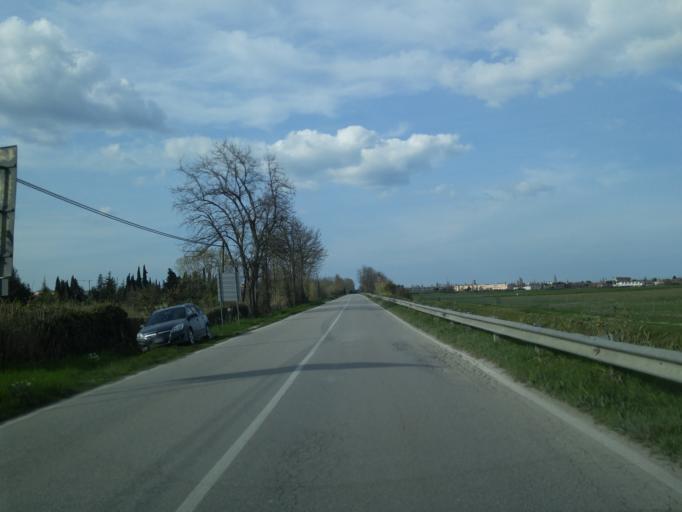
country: IT
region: The Marches
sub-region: Provincia di Pesaro e Urbino
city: Rosciano
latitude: 43.8196
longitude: 13.0170
